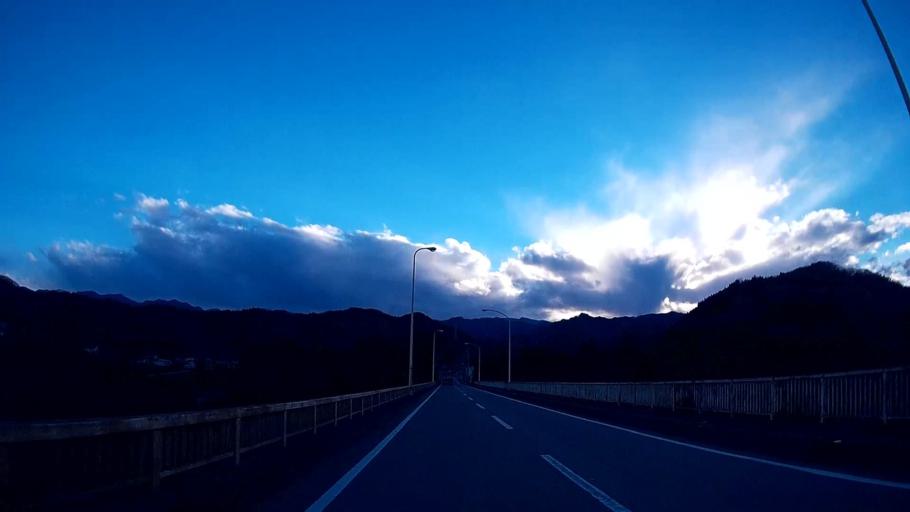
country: JP
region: Saitama
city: Chichibu
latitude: 36.0282
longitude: 138.9879
